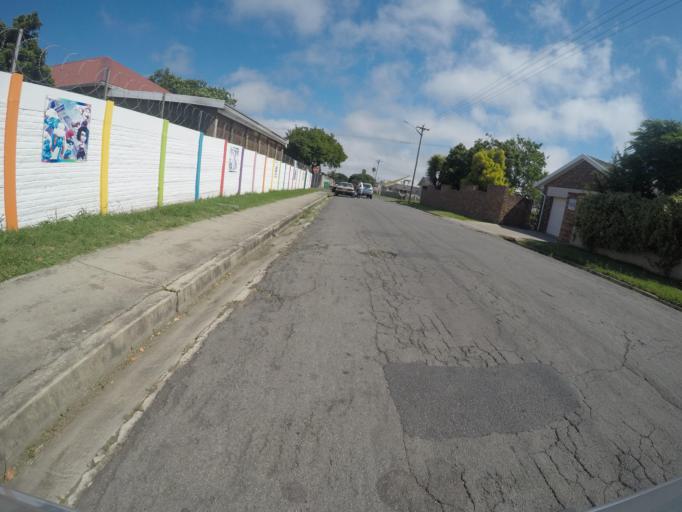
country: ZA
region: Eastern Cape
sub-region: Buffalo City Metropolitan Municipality
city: East London
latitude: -32.9770
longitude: 27.8934
